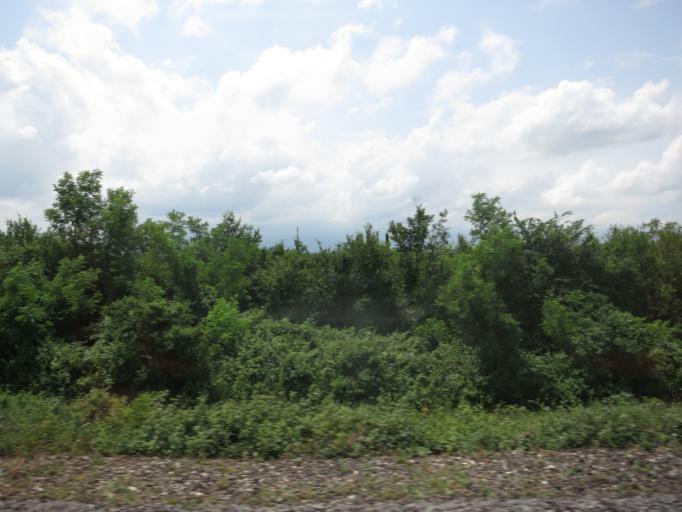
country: GE
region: Imereti
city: Kutaisi
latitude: 42.1998
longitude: 42.6498
